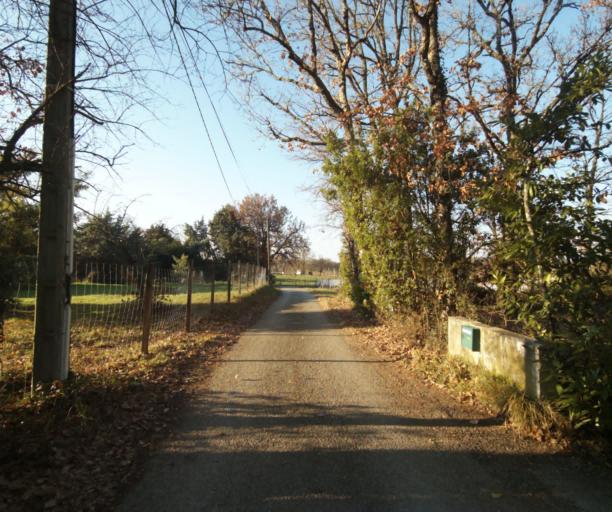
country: FR
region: Midi-Pyrenees
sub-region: Departement du Tarn-et-Garonne
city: Moissac
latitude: 44.1432
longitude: 1.1229
